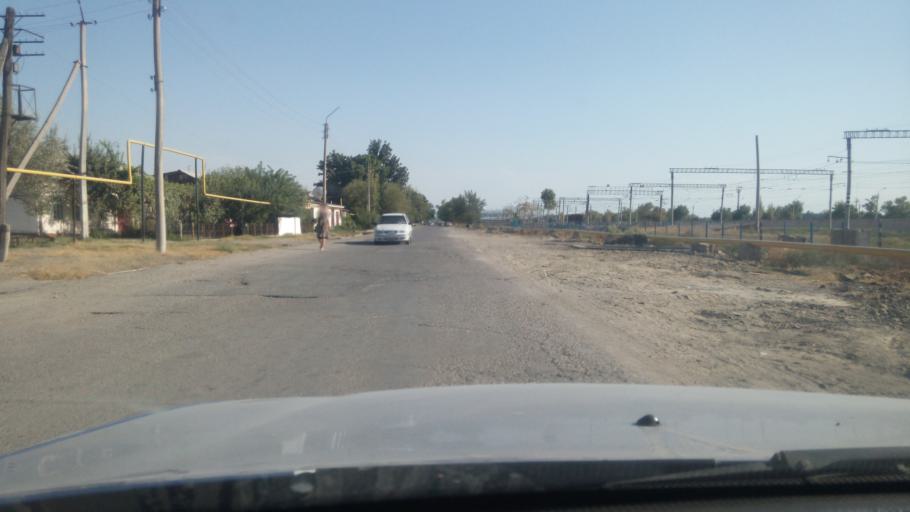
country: UZ
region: Sirdaryo
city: Guliston
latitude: 40.5052
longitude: 68.7625
